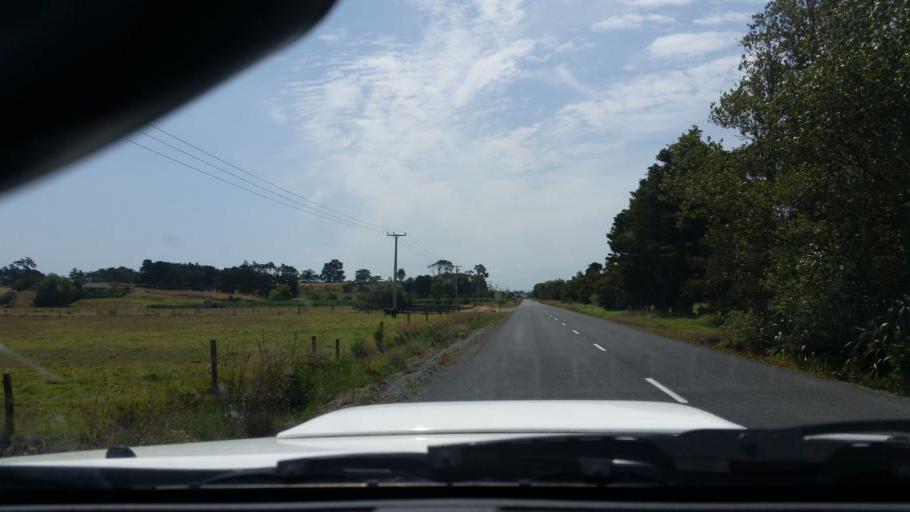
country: NZ
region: Northland
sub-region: Kaipara District
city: Dargaville
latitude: -36.0649
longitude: 173.9388
